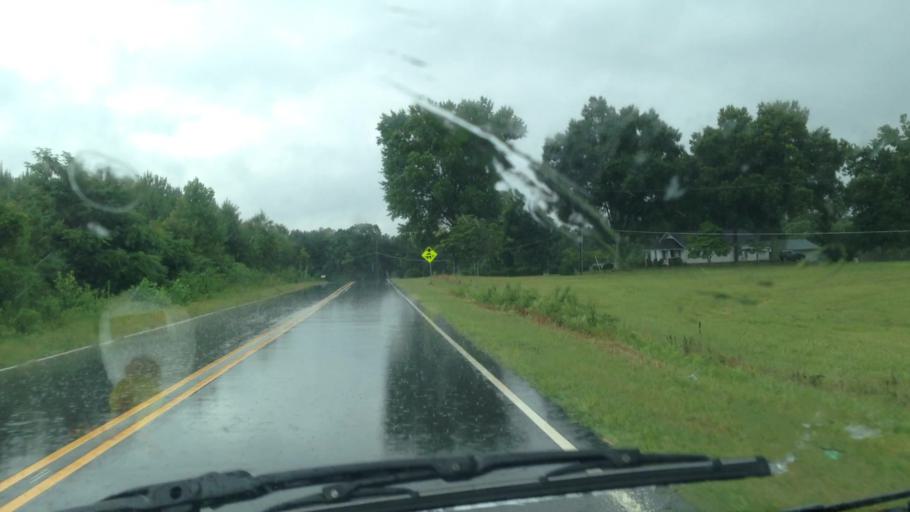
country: US
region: North Carolina
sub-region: Stokes County
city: Danbury
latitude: 36.4268
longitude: -80.0886
